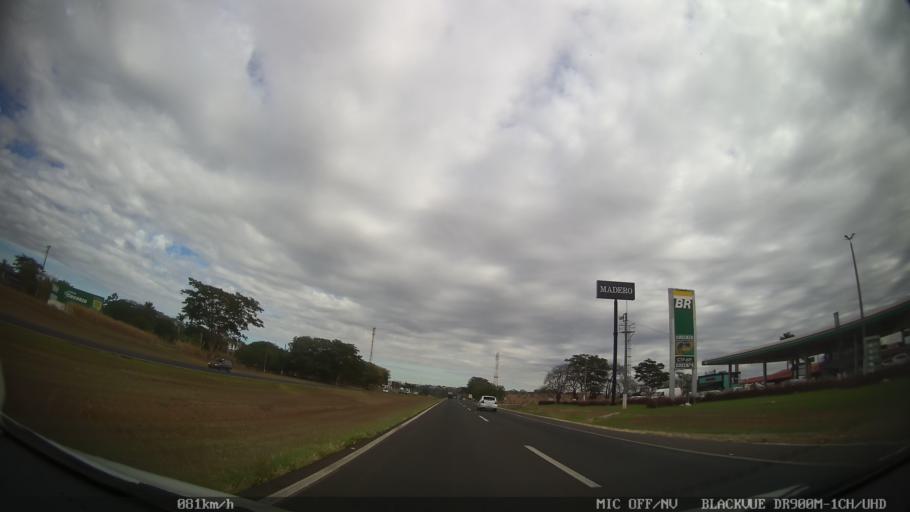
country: BR
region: Sao Paulo
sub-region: Sao Jose Do Rio Preto
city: Sao Jose do Rio Preto
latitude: -20.8154
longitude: -49.4579
